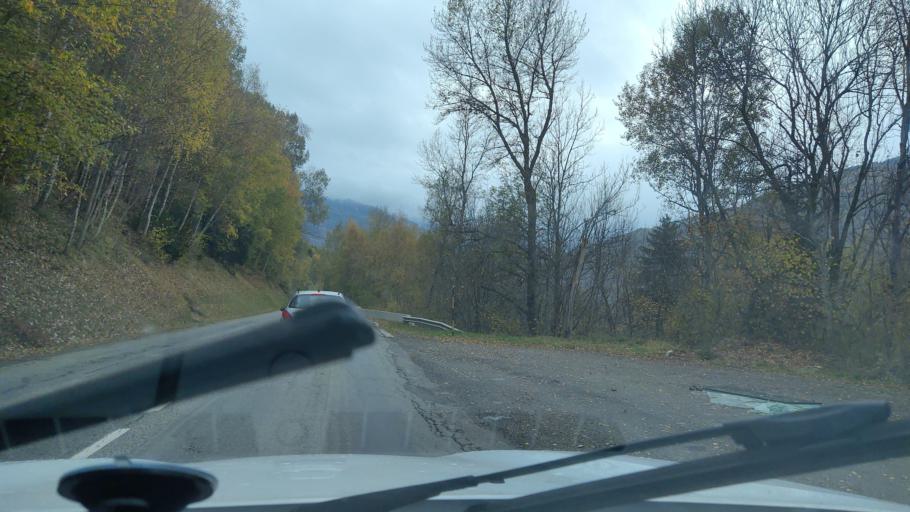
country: FR
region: Rhone-Alpes
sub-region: Departement de la Savoie
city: Bourg-Saint-Maurice
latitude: 45.6037
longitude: 6.7759
